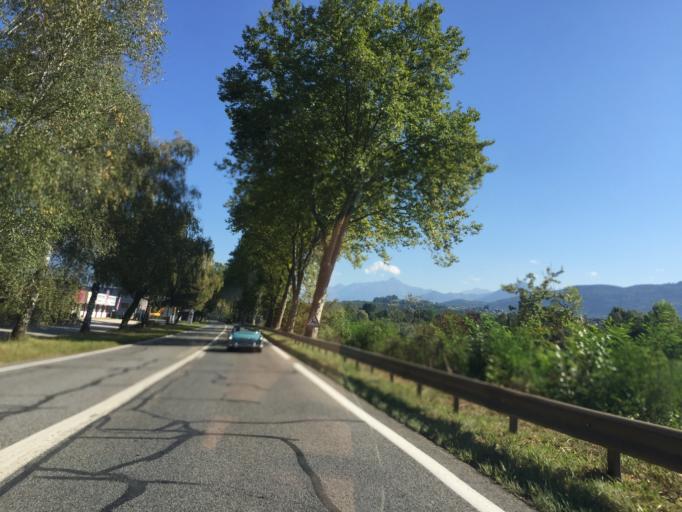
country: FR
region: Rhone-Alpes
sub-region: Departement de la Savoie
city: Montmelian
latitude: 45.5053
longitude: 6.0767
